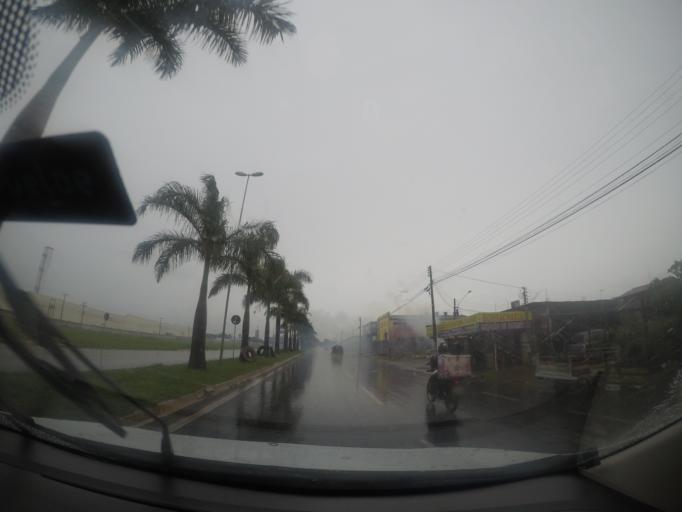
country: BR
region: Goias
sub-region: Goiania
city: Goiania
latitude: -16.6451
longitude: -49.3131
